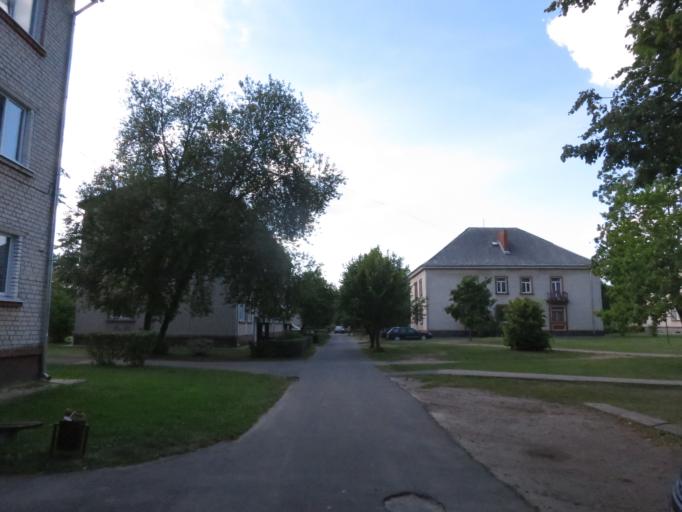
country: LV
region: Incukalns
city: Vangazi
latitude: 57.0911
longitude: 24.5461
